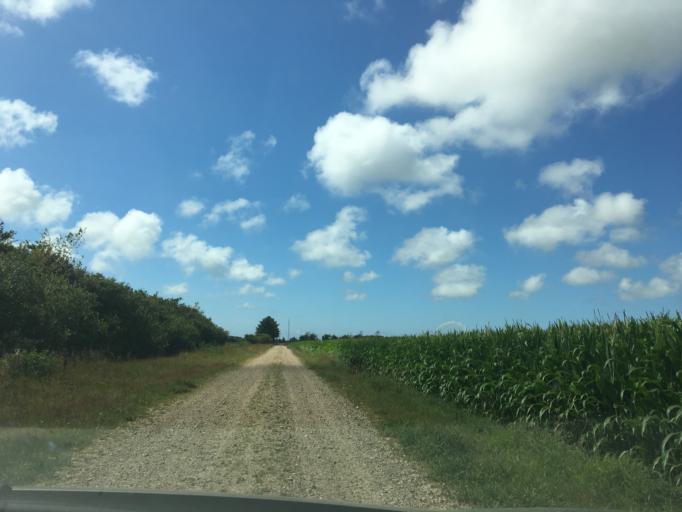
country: DK
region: South Denmark
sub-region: Varde Kommune
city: Oksbol
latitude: 55.8134
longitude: 8.2825
